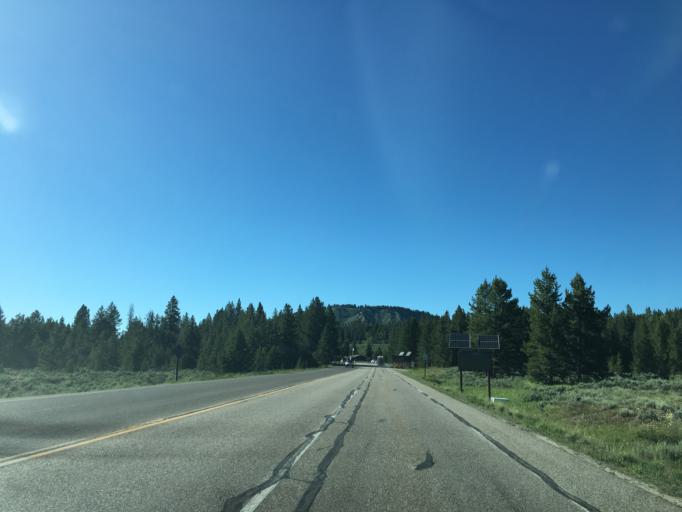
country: US
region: Wyoming
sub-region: Teton County
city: Jackson
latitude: 43.8409
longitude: -110.5104
